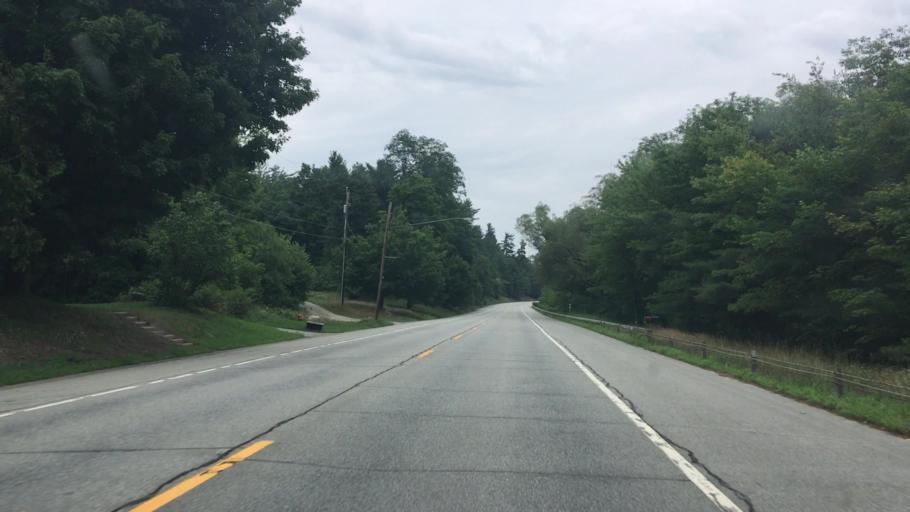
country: US
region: New York
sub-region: Essex County
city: Elizabethtown
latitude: 44.3435
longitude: -73.7674
